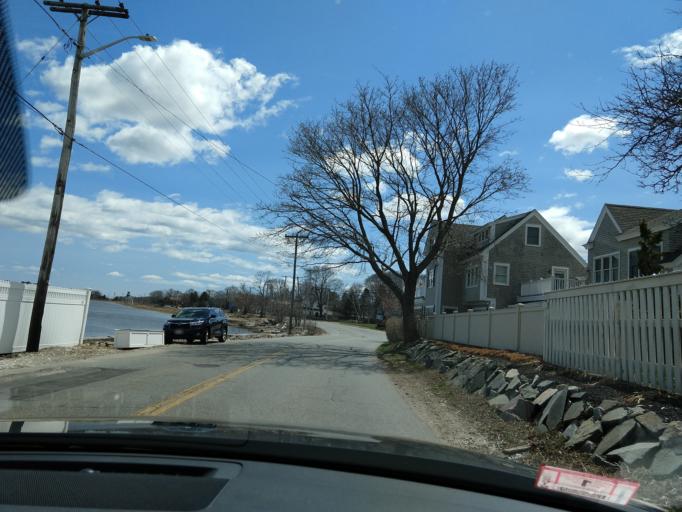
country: US
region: Massachusetts
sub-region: Essex County
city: Newburyport
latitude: 42.8035
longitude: -70.8537
